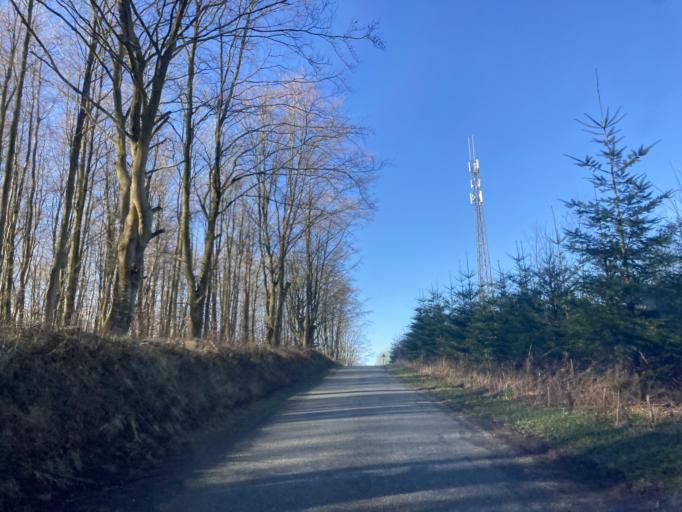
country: DK
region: Zealand
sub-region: Ringsted Kommune
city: Ringsted
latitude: 55.5008
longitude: 11.8416
